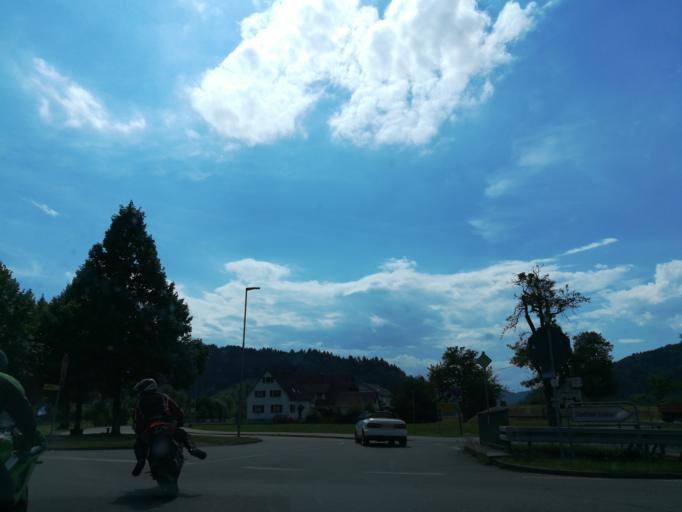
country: DE
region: Baden-Wuerttemberg
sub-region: Freiburg Region
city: Hausach
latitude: 48.2860
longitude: 8.1663
